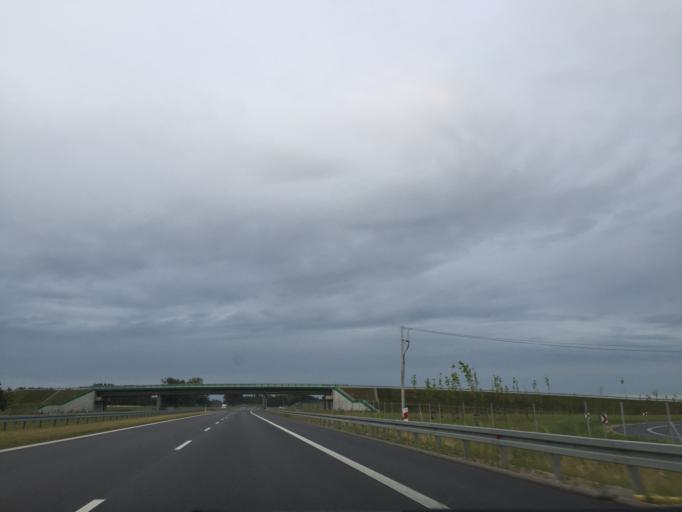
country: PL
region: Podlasie
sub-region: Powiat zambrowski
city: Rutki-Kossaki
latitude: 53.0792
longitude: 22.4432
